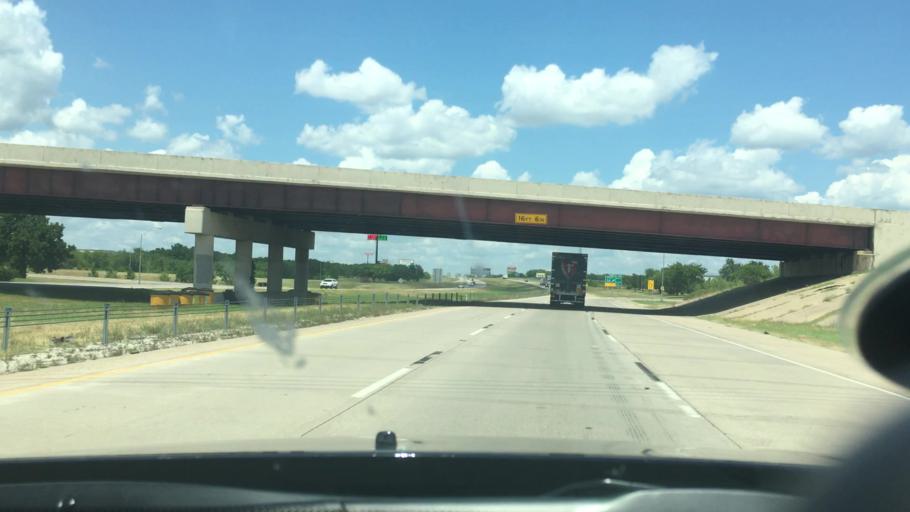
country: US
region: Oklahoma
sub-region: Carter County
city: Ardmore
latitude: 34.1870
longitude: -97.1663
